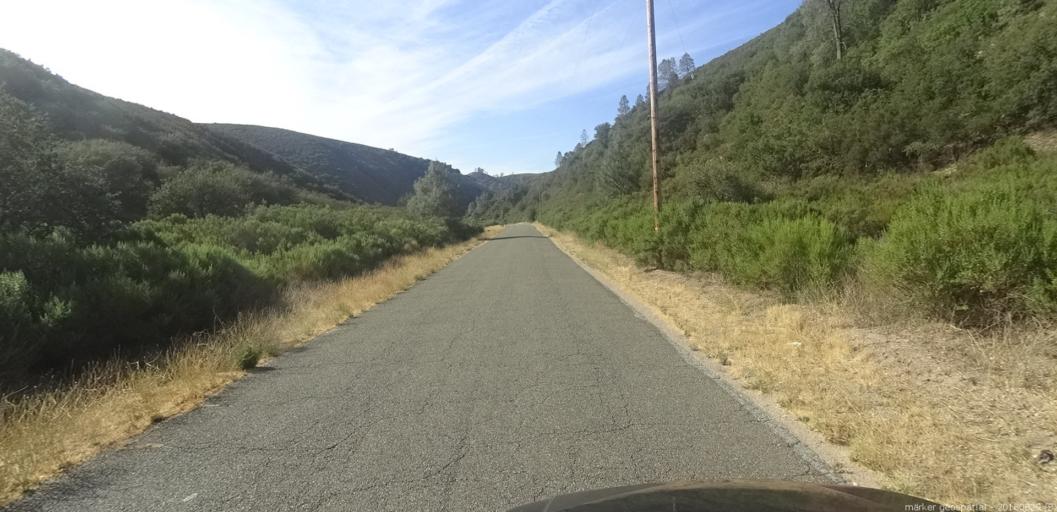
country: US
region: California
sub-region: Monterey County
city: King City
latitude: 36.0115
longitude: -121.0679
